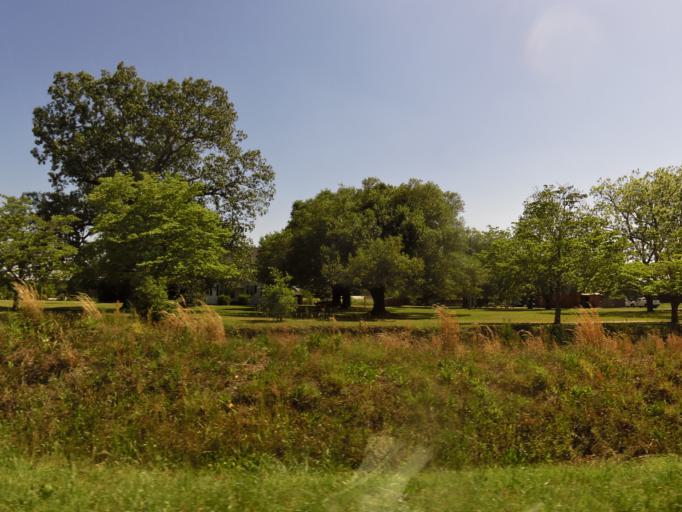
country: US
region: South Carolina
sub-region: Aiken County
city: Aiken
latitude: 33.5237
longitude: -81.6177
